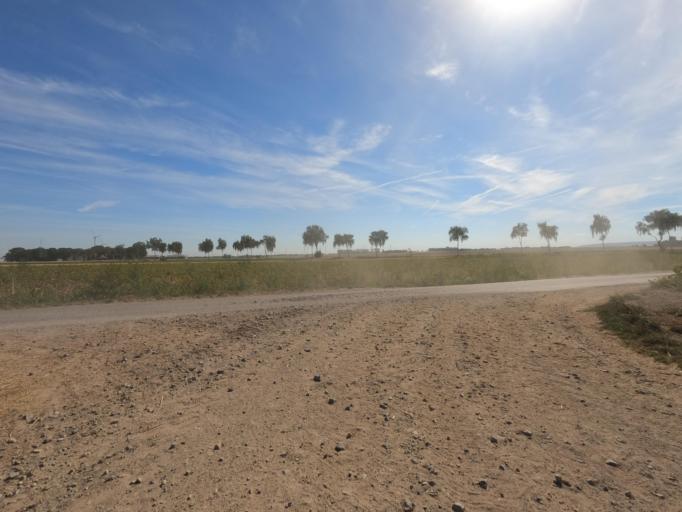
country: DE
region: North Rhine-Westphalia
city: Erkelenz
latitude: 51.0381
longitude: 6.3606
